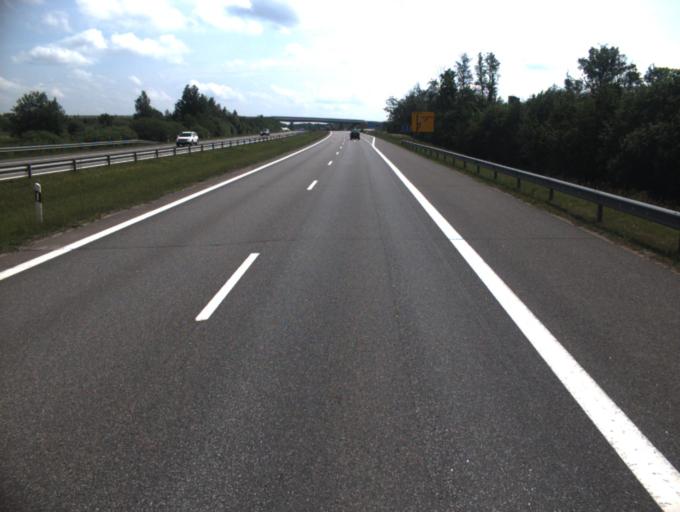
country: LT
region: Klaipedos apskritis
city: Gargzdai
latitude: 55.7100
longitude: 21.4728
